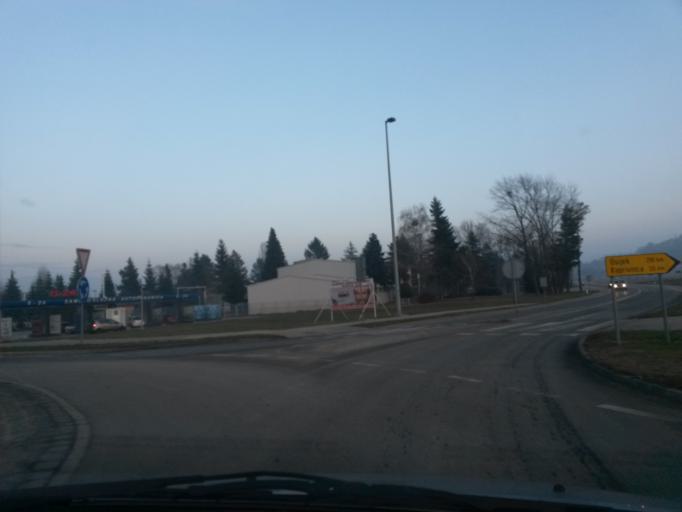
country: HR
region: Varazdinska
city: Ludbreg
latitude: 46.2419
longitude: 16.6290
